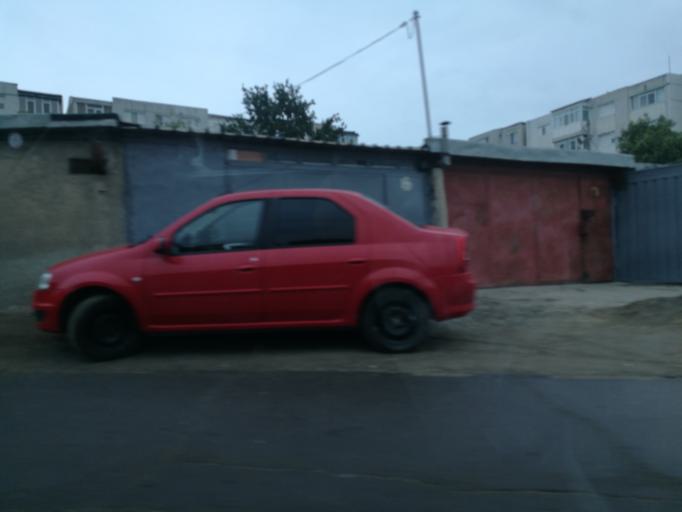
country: RO
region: Galati
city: Galati
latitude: 45.4500
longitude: 28.0157
